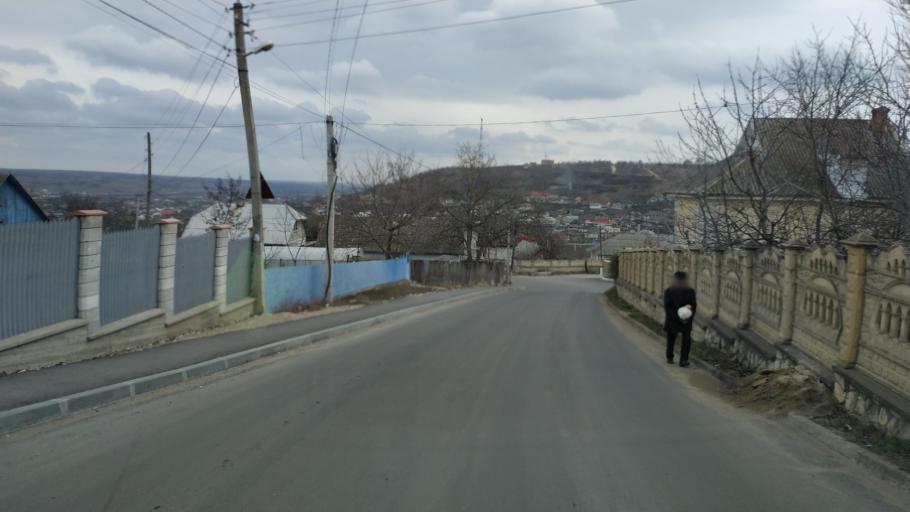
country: MD
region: Laloveni
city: Ialoveni
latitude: 46.8688
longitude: 28.7575
